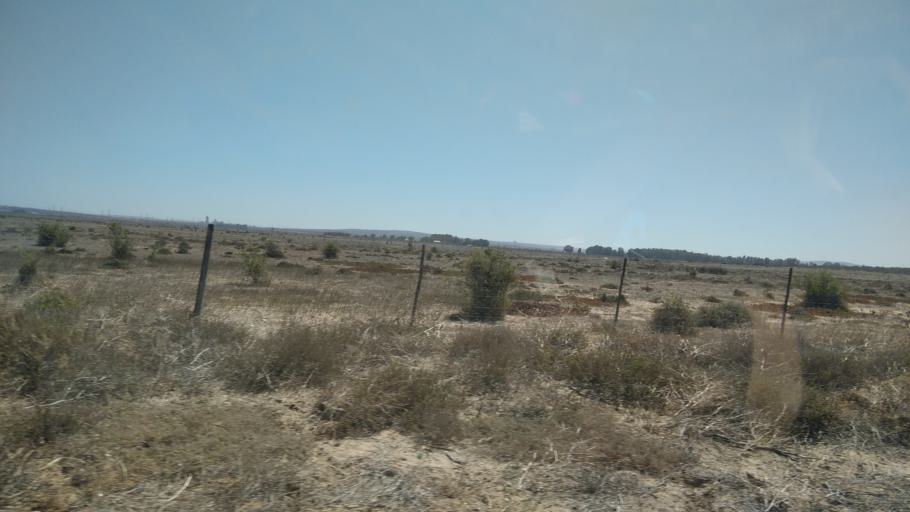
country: ZA
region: Western Cape
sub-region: West Coast District Municipality
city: Vredenburg
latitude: -33.0187
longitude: 18.1113
